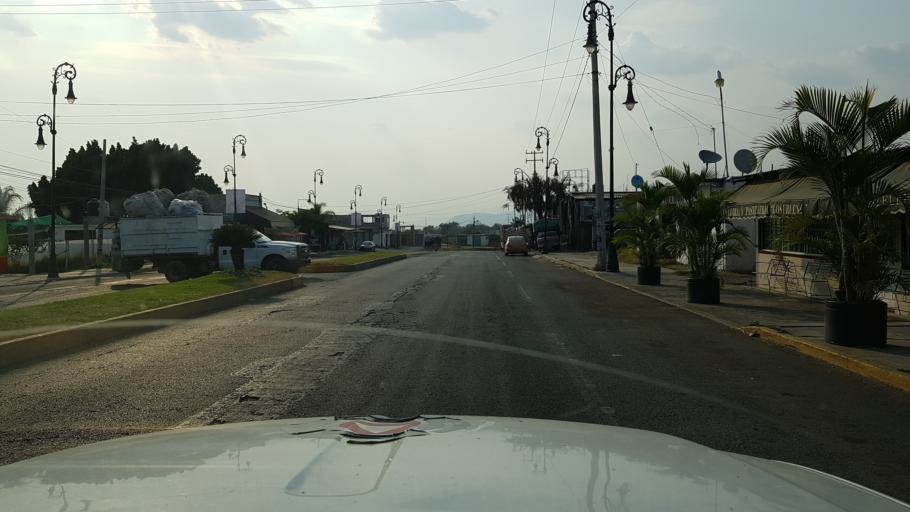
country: MX
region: Morelos
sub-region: Yecapixtla
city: Yecapixtla
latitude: 18.8863
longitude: -98.8726
